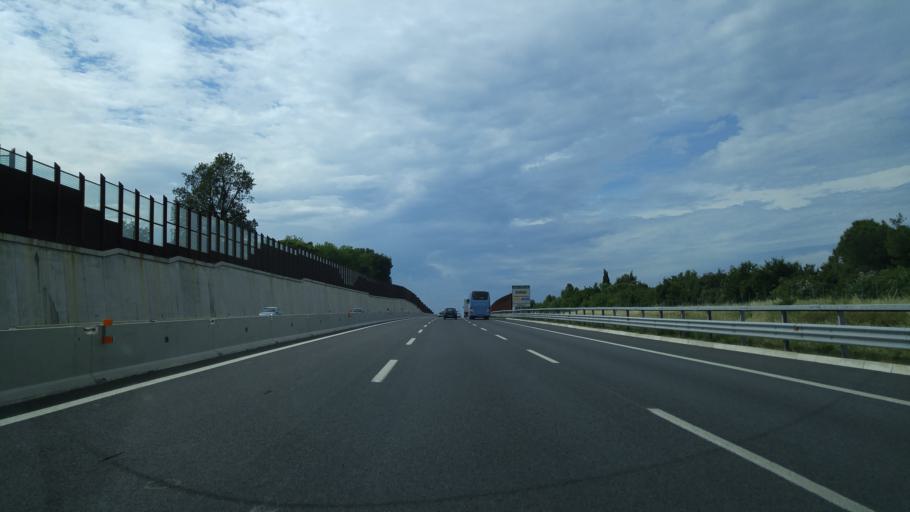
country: IT
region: Emilia-Romagna
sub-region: Provincia di Rimini
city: Rivazzurra
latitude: 44.0181
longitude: 12.5862
